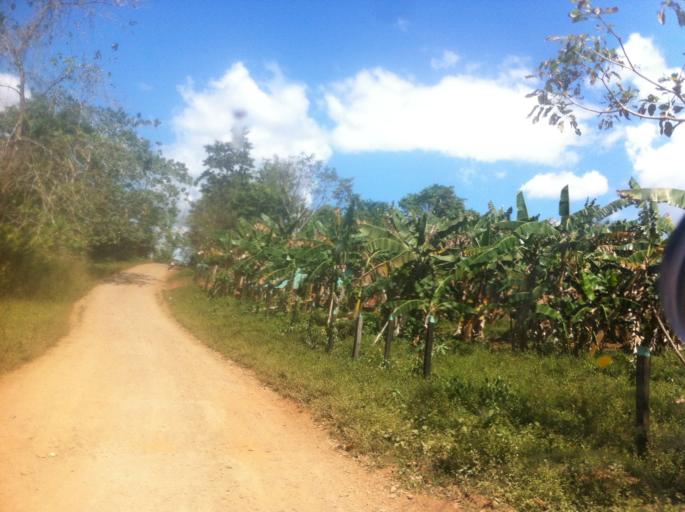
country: CR
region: Alajuela
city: Los Chiles
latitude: 11.2369
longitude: -84.4825
